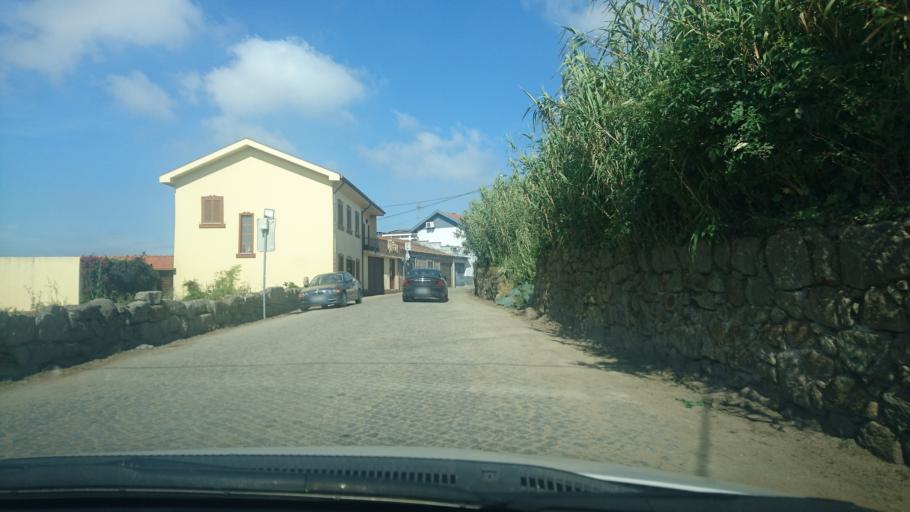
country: PT
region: Porto
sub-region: Matosinhos
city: Lavra
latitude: 41.2676
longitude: -8.7124
